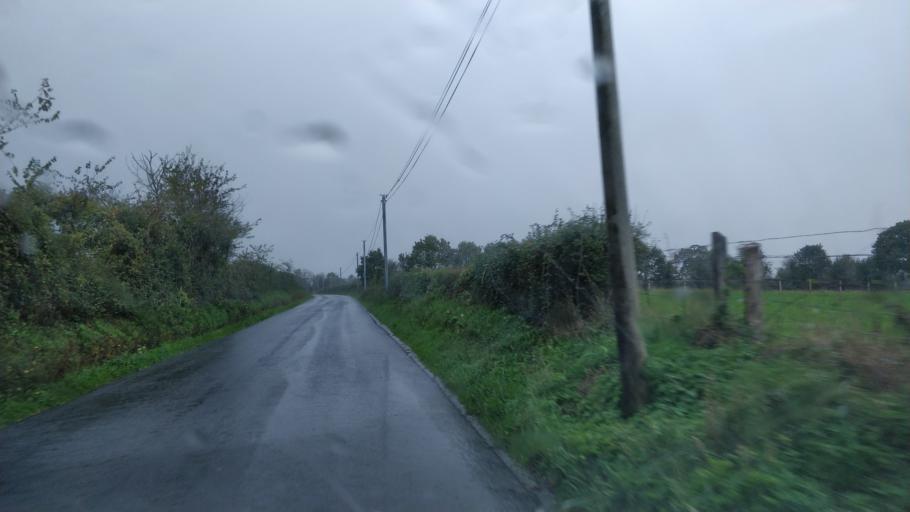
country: FR
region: Lower Normandy
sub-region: Departement de la Manche
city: Brehal
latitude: 48.9013
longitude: -1.5269
